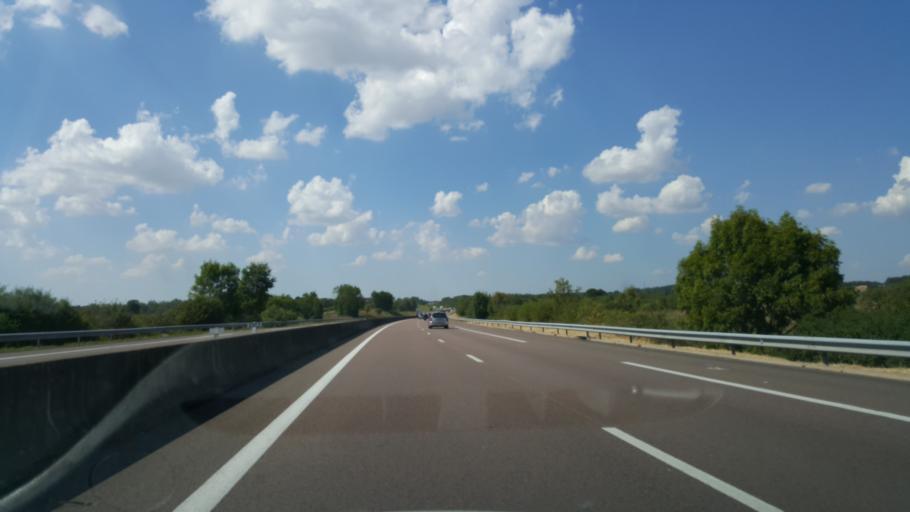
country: FR
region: Bourgogne
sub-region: Departement de la Cote-d'Or
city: Semur-en-Auxois
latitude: 47.4234
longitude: 4.3227
